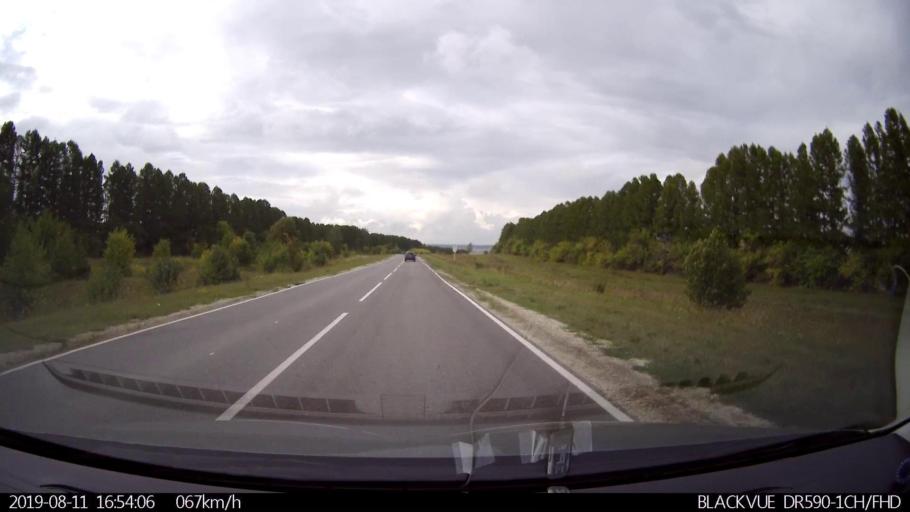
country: RU
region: Ulyanovsk
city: Mayna
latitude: 54.2693
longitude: 47.6673
